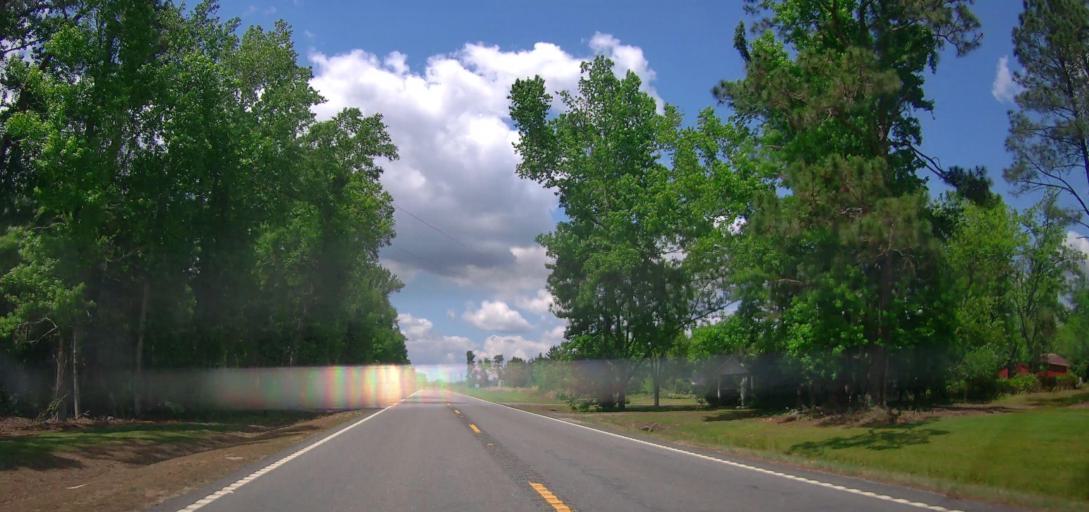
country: US
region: Georgia
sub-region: Treutlen County
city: Soperton
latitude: 32.3969
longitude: -82.6027
